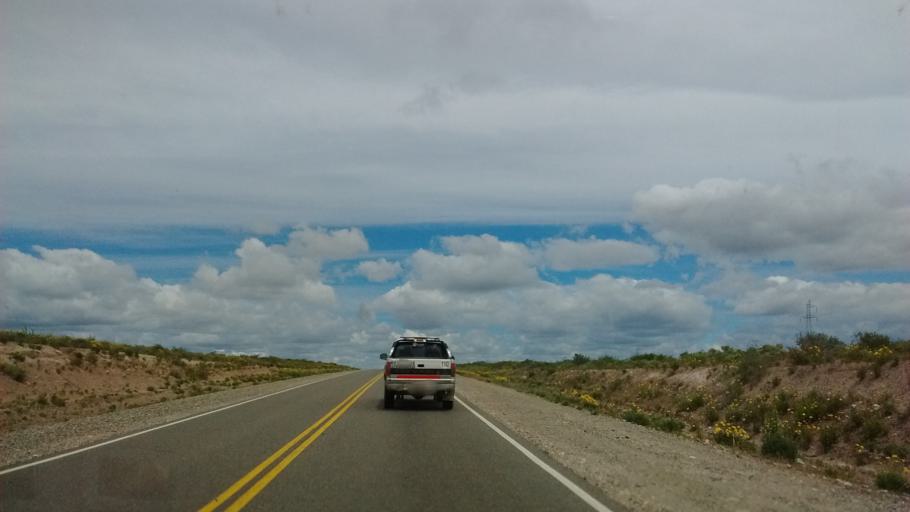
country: AR
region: Neuquen
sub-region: Departamento de Picun Leufu
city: Picun Leufu
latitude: -39.7364
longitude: -69.5916
